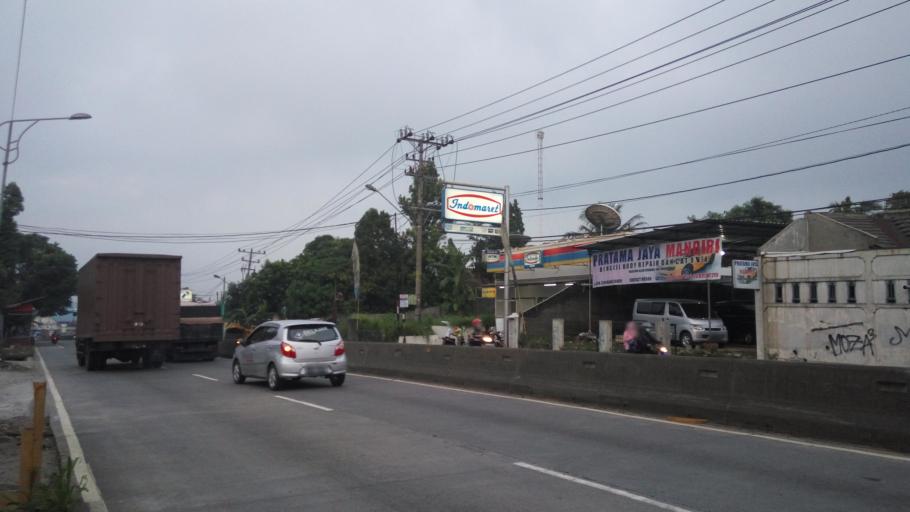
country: ID
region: Central Java
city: Ambarawa
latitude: -7.2192
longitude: 110.4301
